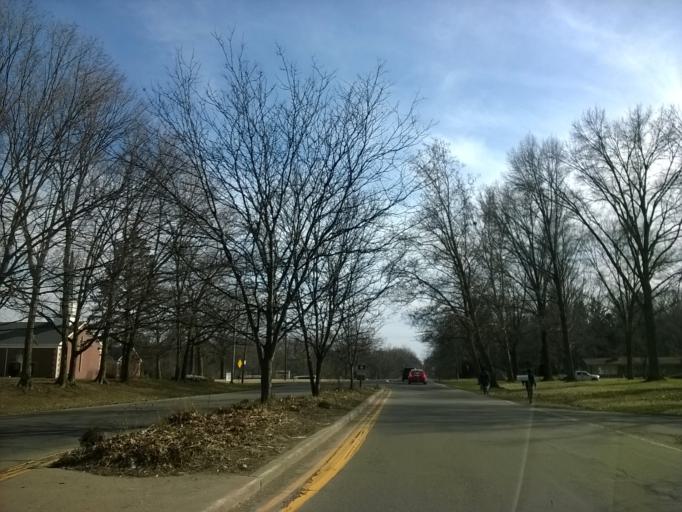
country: US
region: Indiana
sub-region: Marion County
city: Speedway
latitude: 39.8210
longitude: -86.2113
